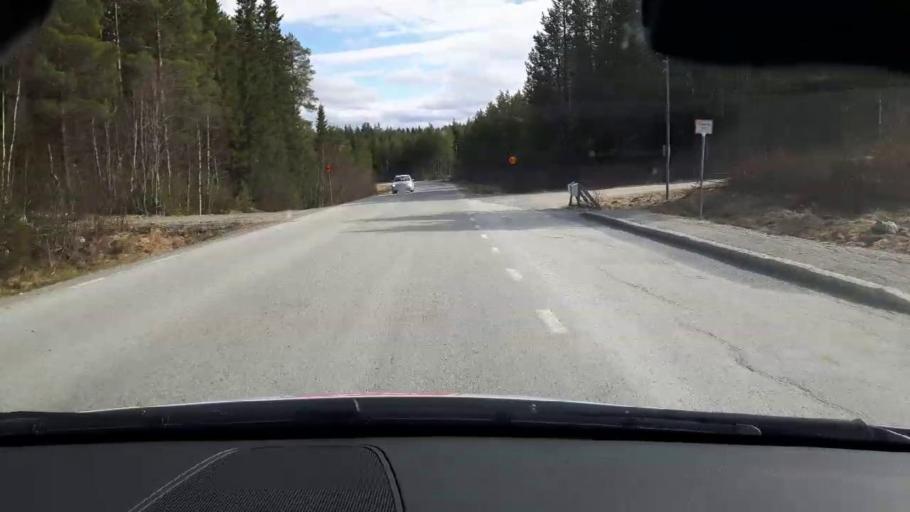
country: SE
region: Jaemtland
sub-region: Bergs Kommun
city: Hoverberg
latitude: 62.7229
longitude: 14.6006
